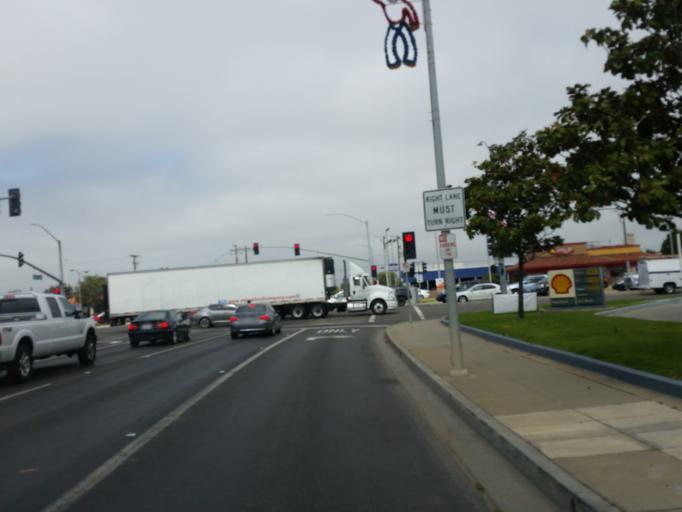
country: US
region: California
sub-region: Santa Barbara County
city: Santa Maria
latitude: 34.9209
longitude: -120.4354
